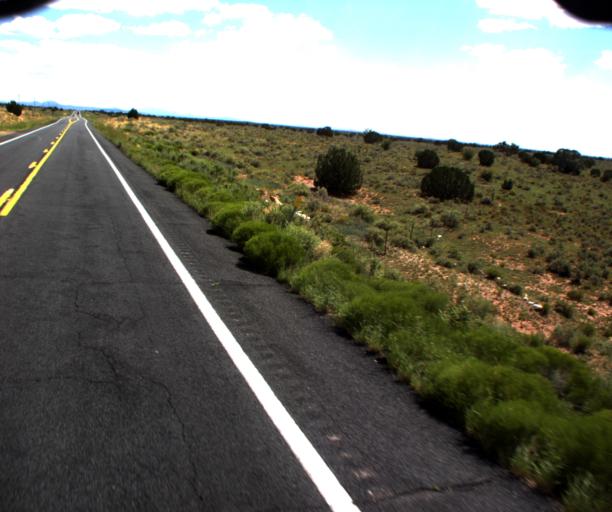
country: US
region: Arizona
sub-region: Coconino County
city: Grand Canyon Village
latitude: 35.7338
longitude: -112.1311
